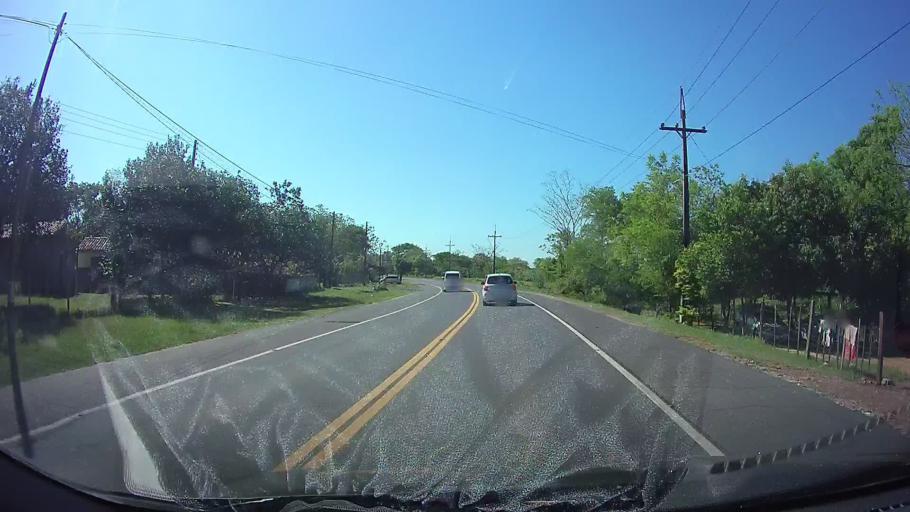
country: PY
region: Central
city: Ypacarai
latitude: -25.3939
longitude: -57.2937
